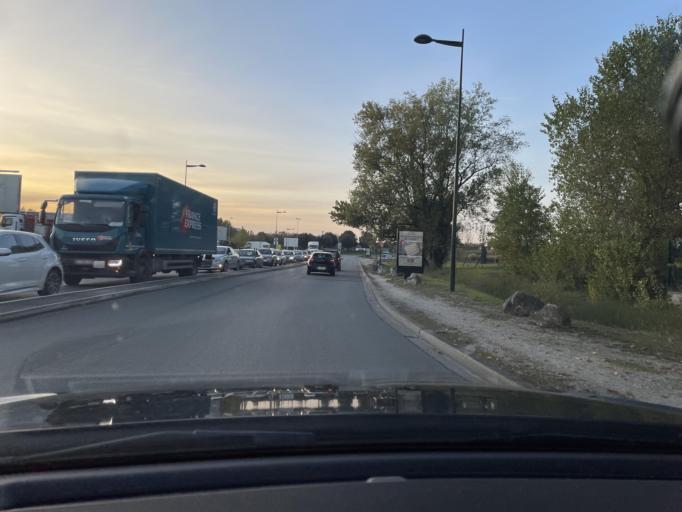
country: FR
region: Aquitaine
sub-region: Departement de la Gironde
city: Villenave-d'Ornon
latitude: 44.7911
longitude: -0.5360
